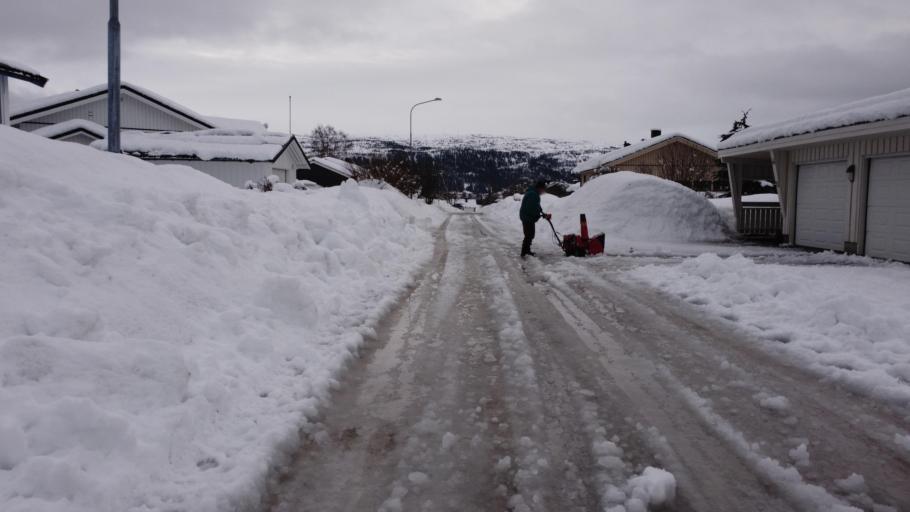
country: NO
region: Nordland
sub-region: Rana
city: Mo i Rana
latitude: 66.3340
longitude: 14.1536
